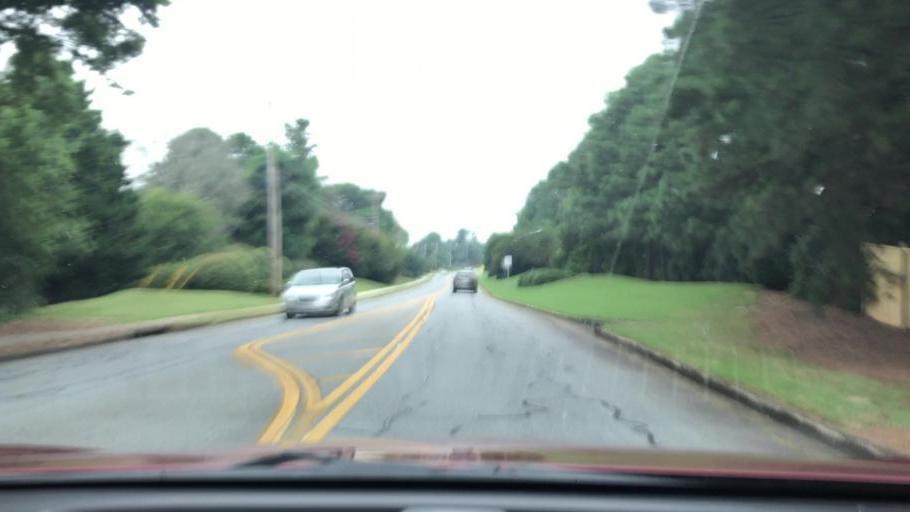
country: US
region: Georgia
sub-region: Gwinnett County
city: Suwanee
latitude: 34.0121
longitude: -84.0241
